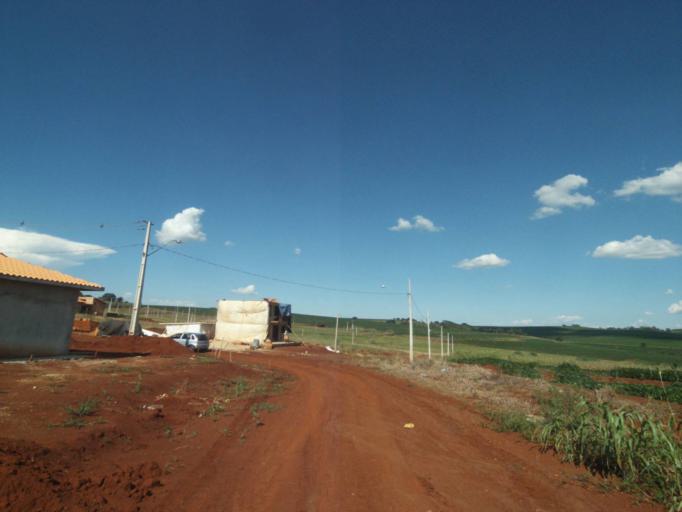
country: BR
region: Parana
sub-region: Sertanopolis
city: Sertanopolis
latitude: -23.0481
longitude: -50.8178
